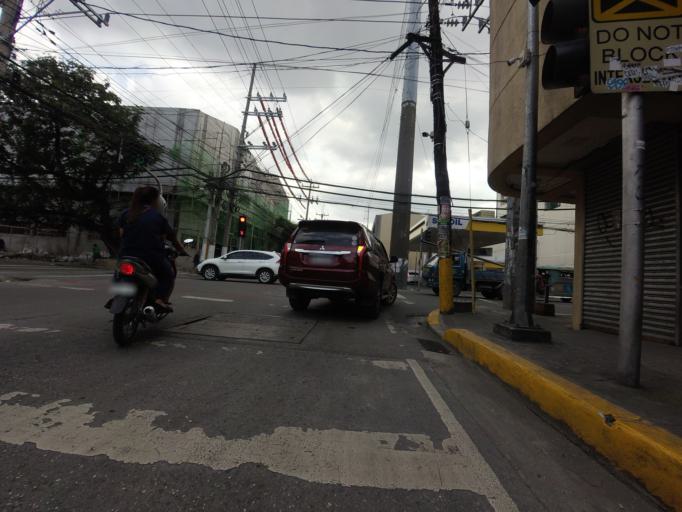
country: PH
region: Metro Manila
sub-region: City of Manila
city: Quiapo
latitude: 14.5818
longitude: 120.9972
